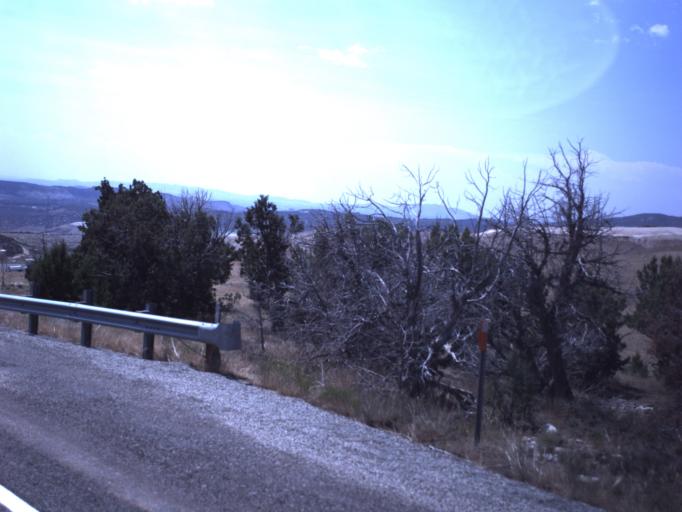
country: US
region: Utah
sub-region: Uintah County
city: Vernal
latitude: 40.6286
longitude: -109.4761
